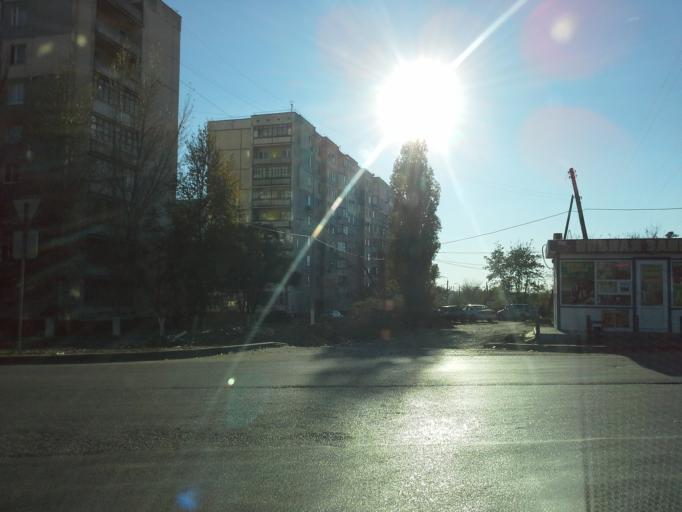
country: RU
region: Volgograd
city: Vodstroy
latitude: 48.8194
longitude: 44.6164
